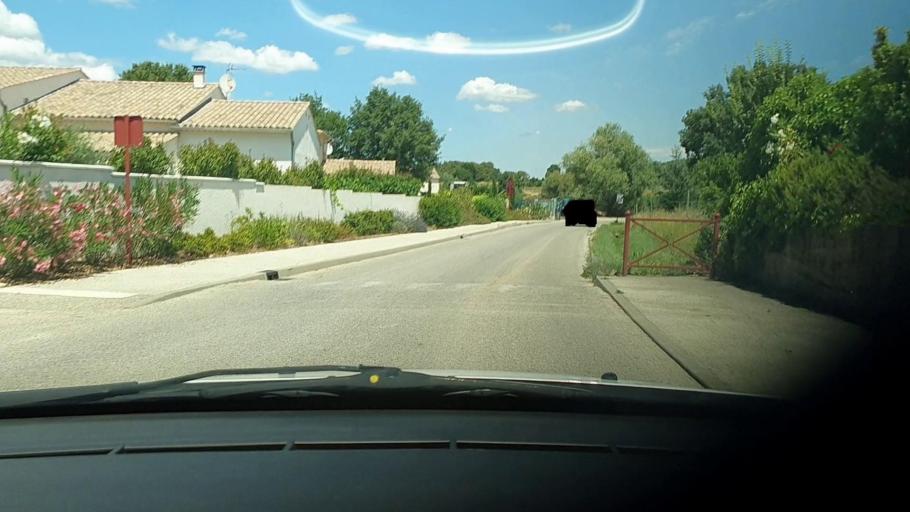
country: FR
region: Languedoc-Roussillon
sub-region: Departement du Gard
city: Blauzac
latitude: 43.9686
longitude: 4.3662
